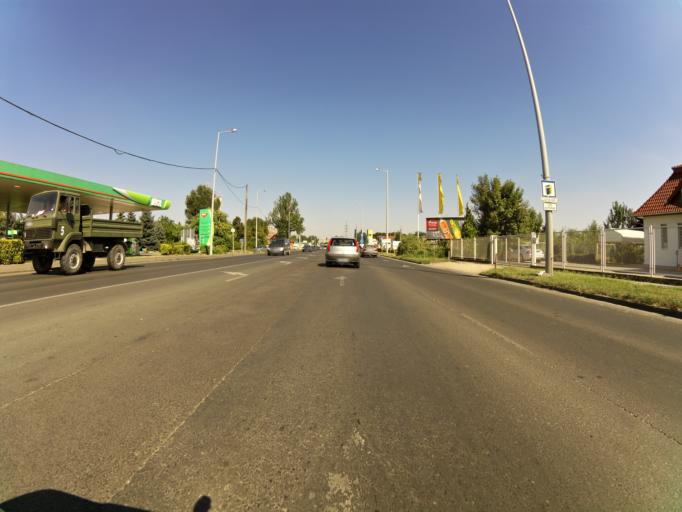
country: HU
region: Csongrad
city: Szeged
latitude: 46.2656
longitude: 20.1149
